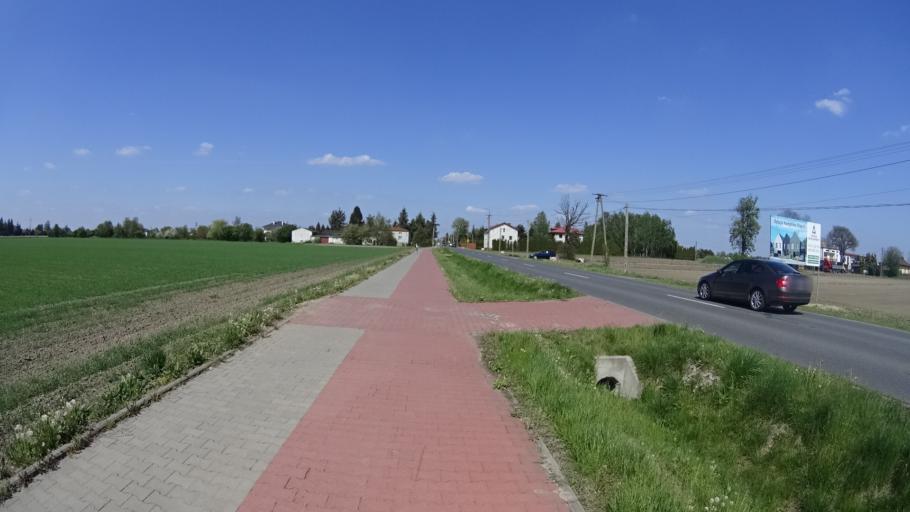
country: PL
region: Masovian Voivodeship
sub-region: Powiat warszawski zachodni
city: Stare Babice
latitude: 52.2400
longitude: 20.8176
